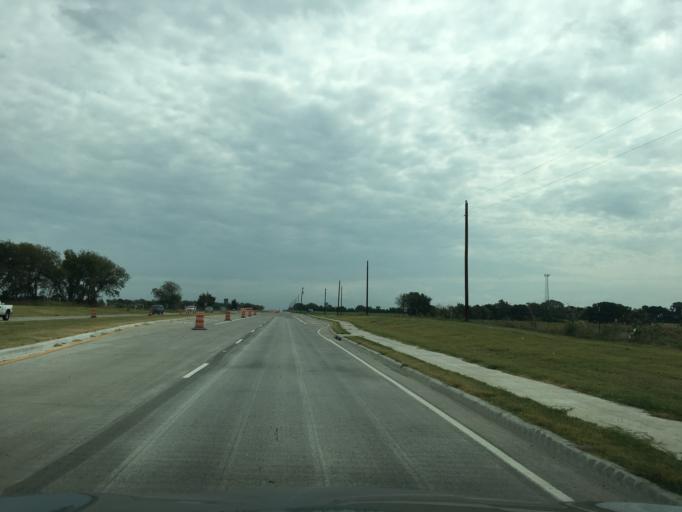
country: US
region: Texas
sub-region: Collin County
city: Anna
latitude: 33.3069
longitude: -96.5215
